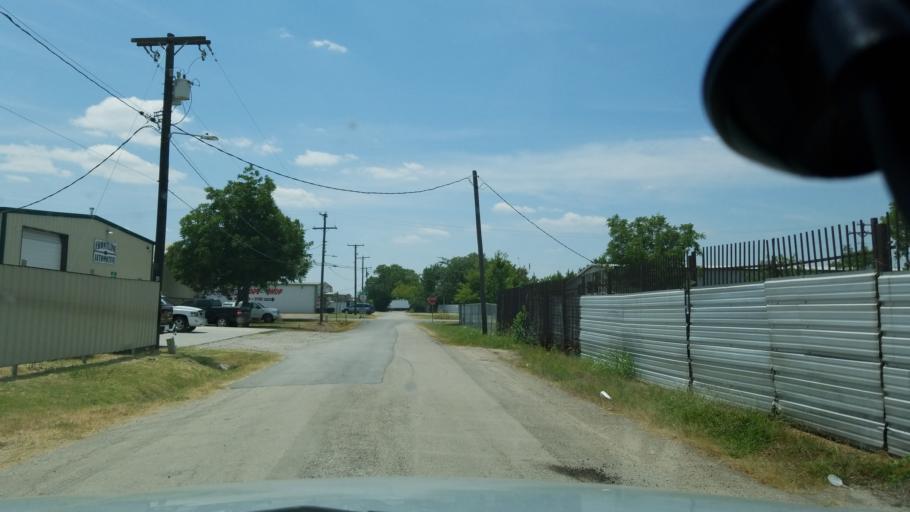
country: US
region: Texas
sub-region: Dallas County
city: Grand Prairie
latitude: 32.7479
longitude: -96.9763
